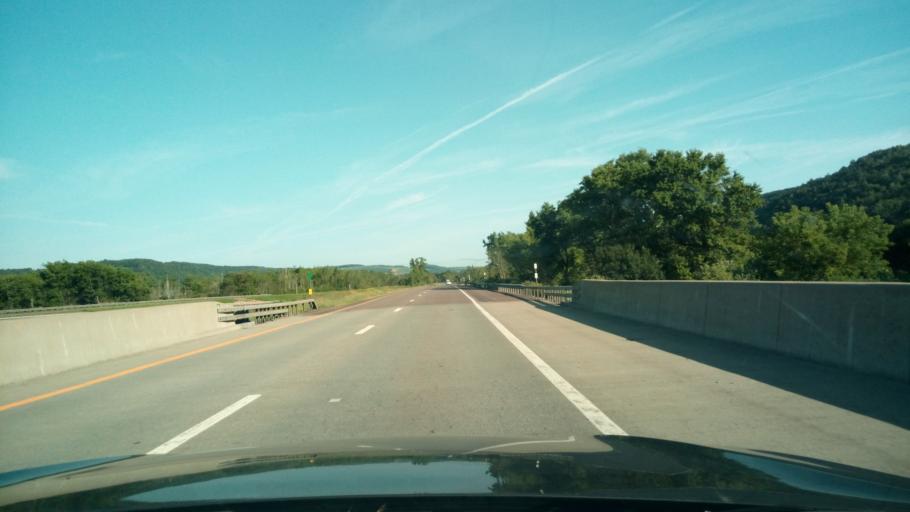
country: US
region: New York
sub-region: Steuben County
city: Bath
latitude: 42.4278
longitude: -77.4358
